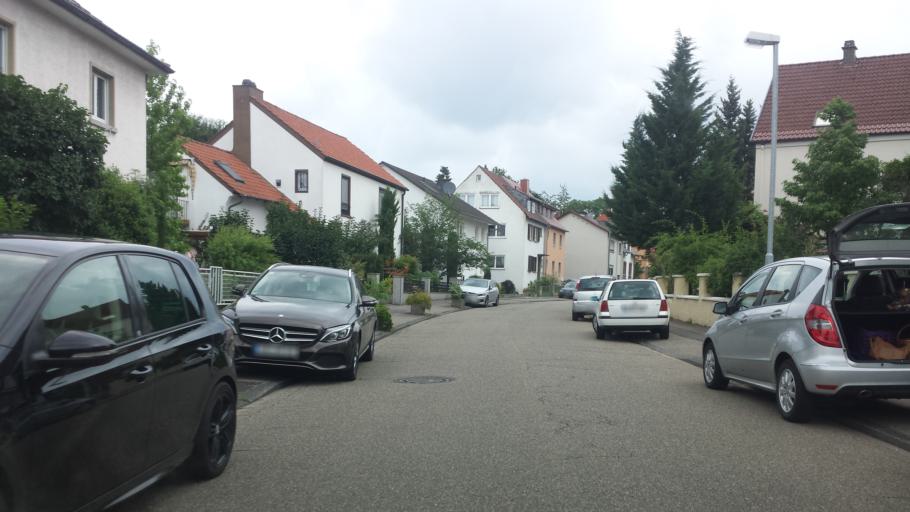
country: DE
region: Rheinland-Pfalz
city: Neustadt
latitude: 49.3429
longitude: 8.1387
